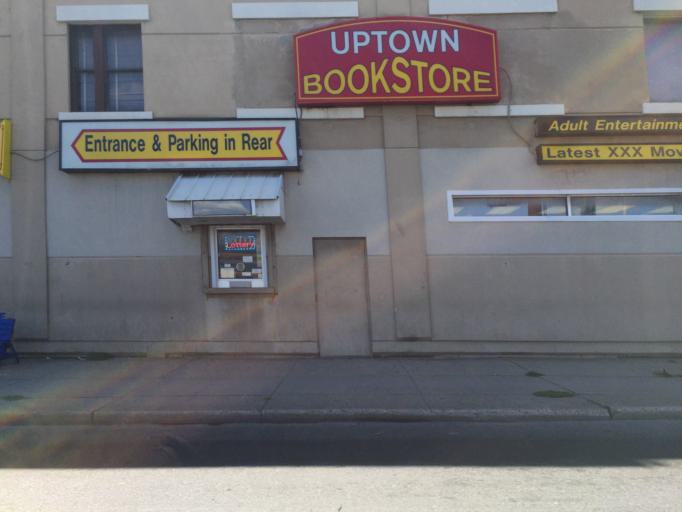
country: US
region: Michigan
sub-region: Wayne County
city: Highland Park
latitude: 42.4175
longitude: -83.1052
